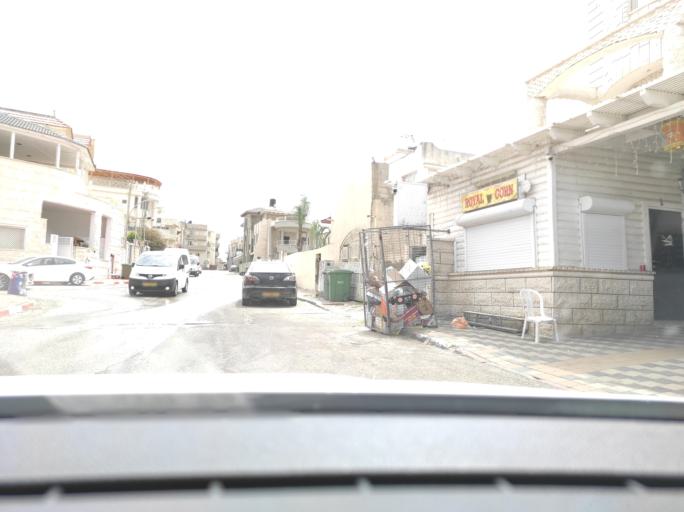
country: IL
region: Central District
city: Kafr Qasim
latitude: 32.1155
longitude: 34.9737
